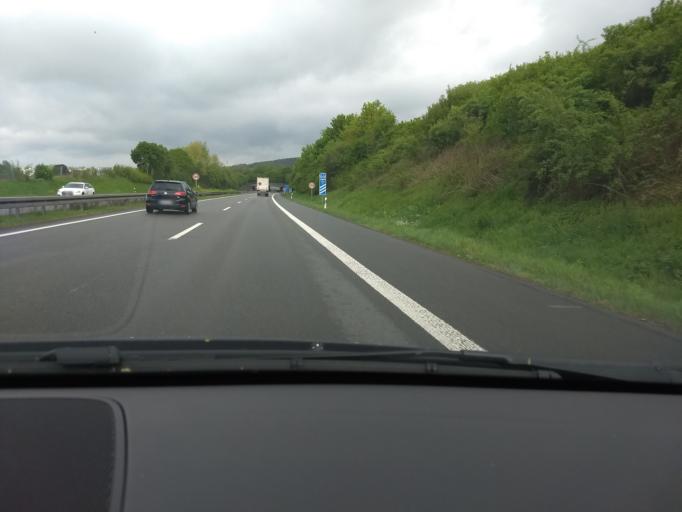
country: DE
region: North Rhine-Westphalia
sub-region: Regierungsbezirk Arnsberg
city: Arnsberg
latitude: 51.3982
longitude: 8.0941
